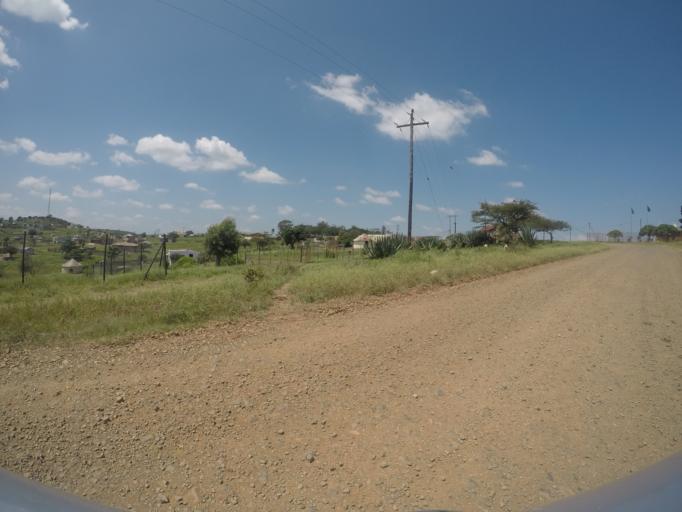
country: ZA
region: KwaZulu-Natal
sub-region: uThungulu District Municipality
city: Empangeni
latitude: -28.6040
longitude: 31.7430
